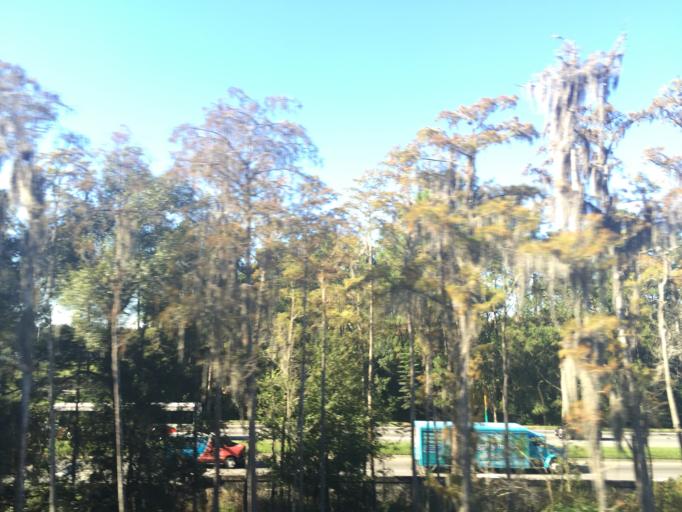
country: US
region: Florida
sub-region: Orange County
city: Bay Hill
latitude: 28.4050
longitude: -81.5757
